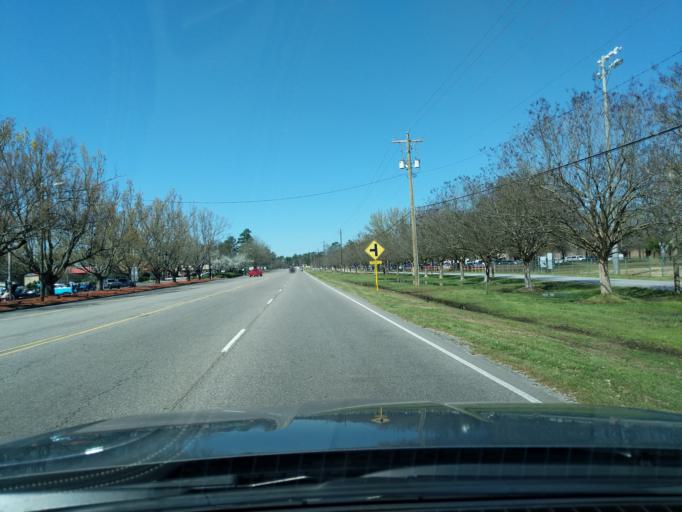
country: US
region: South Carolina
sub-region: Aiken County
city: Aiken
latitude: 33.5253
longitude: -81.7207
